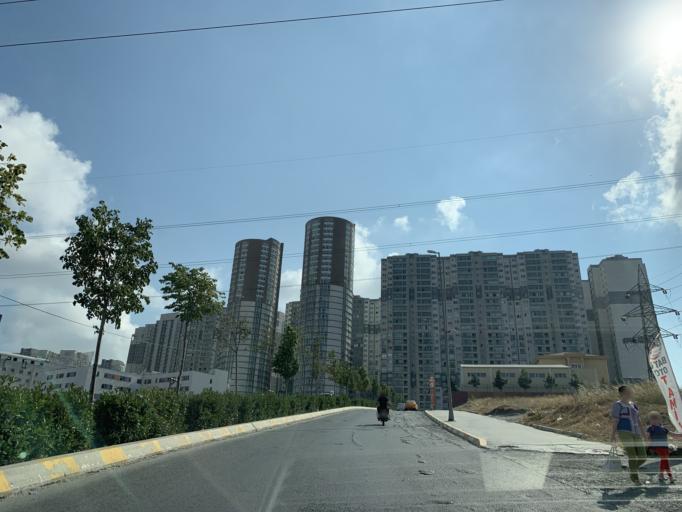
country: TR
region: Istanbul
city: Esenyurt
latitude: 41.0285
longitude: 28.6609
